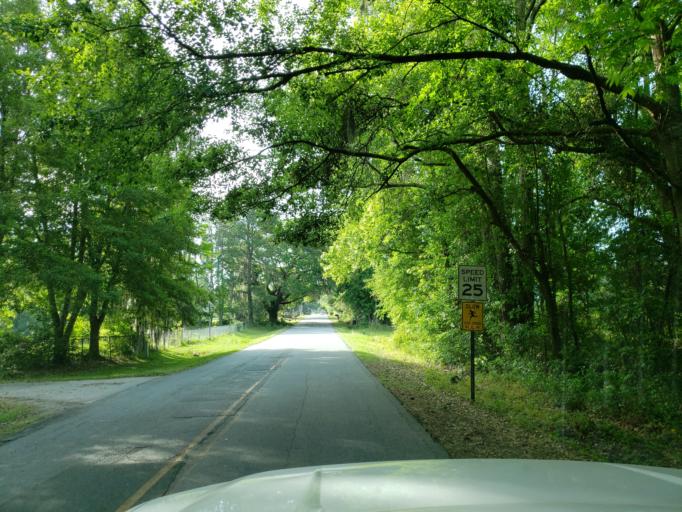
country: US
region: Georgia
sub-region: Chatham County
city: Georgetown
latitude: 32.0116
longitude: -81.2339
